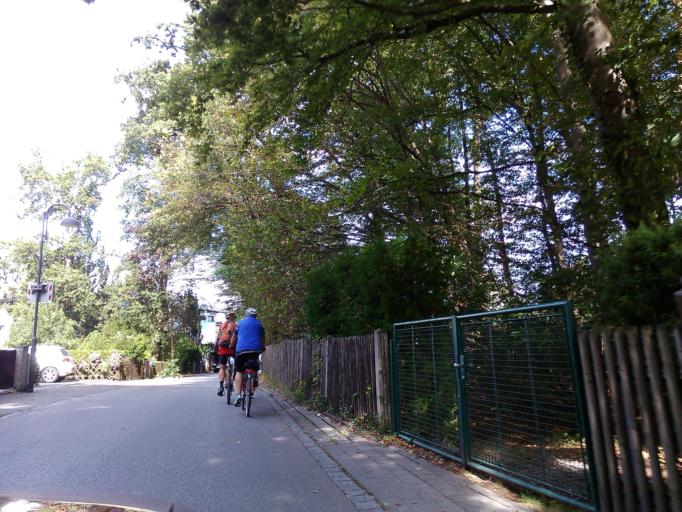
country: DE
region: Bavaria
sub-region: Upper Bavaria
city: Eichenau
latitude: 48.1741
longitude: 11.3322
